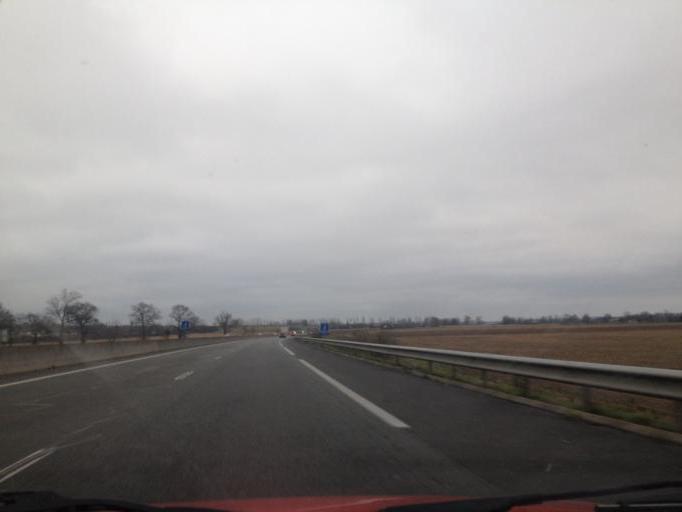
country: FR
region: Auvergne
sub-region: Departement de l'Allier
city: Toulon-sur-Allier
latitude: 46.5113
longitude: 3.3564
